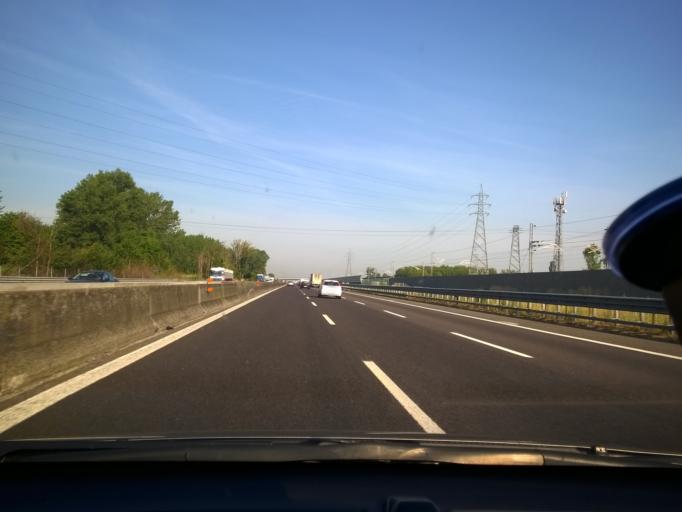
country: IT
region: Emilia-Romagna
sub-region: Provincia di Modena
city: Campogalliano
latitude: 44.6789
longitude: 10.8121
